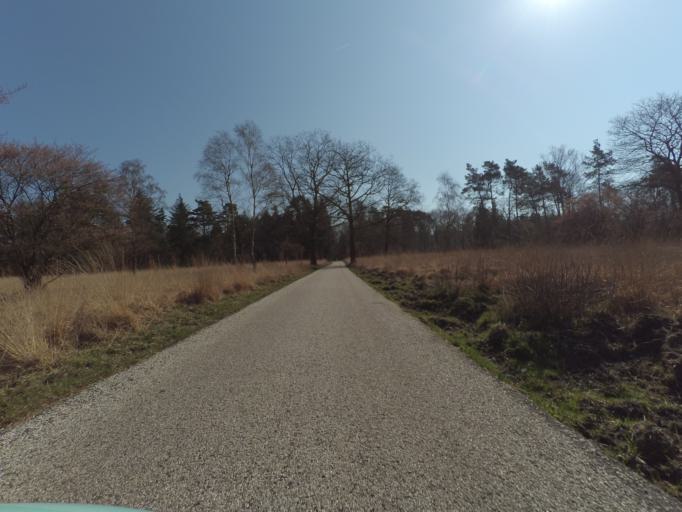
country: NL
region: Gelderland
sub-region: Gemeente Ede
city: Otterlo
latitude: 52.1187
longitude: 5.8562
